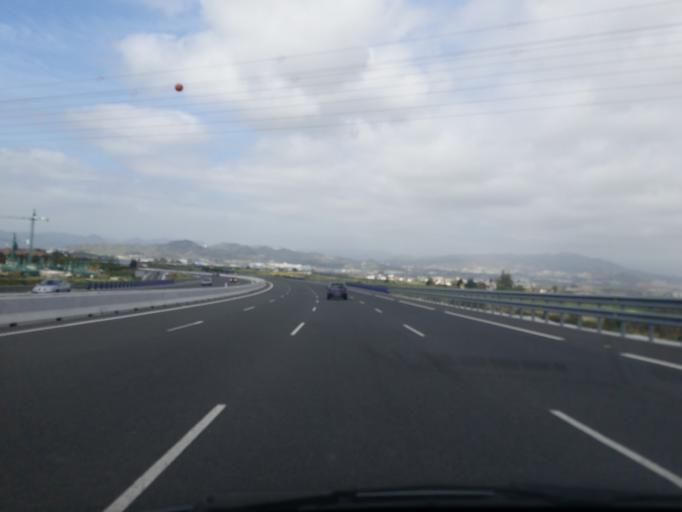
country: ES
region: Andalusia
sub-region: Provincia de Malaga
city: Alhaurin de la Torre
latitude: 36.6758
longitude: -4.5264
